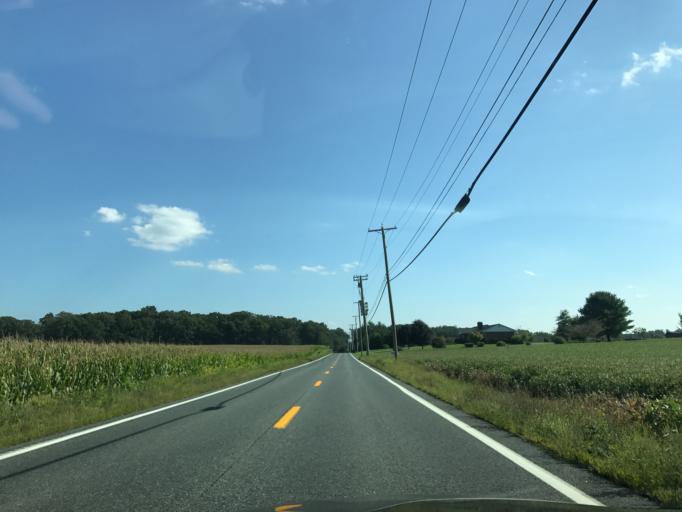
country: US
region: Pennsylvania
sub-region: York County
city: Stewartstown
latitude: 39.6983
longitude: -76.5321
